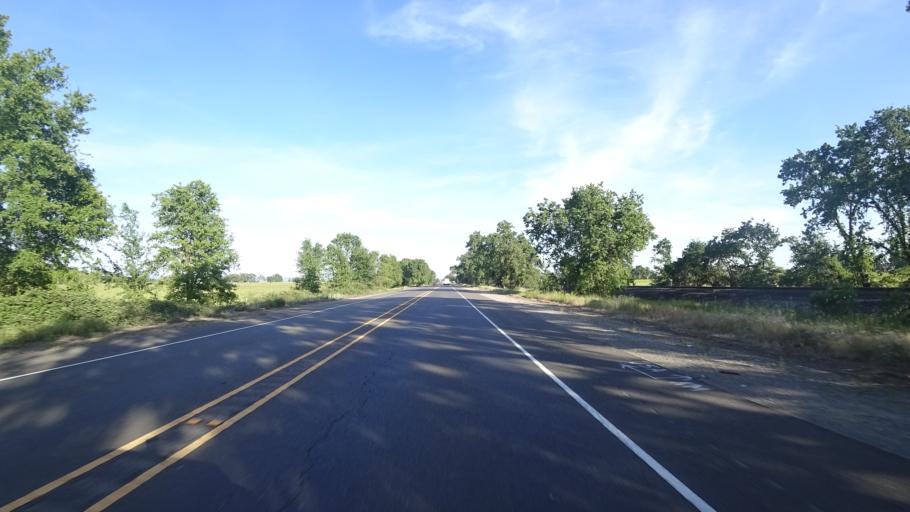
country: US
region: California
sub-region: Placer County
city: Sheridan
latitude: 38.9366
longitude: -121.3494
